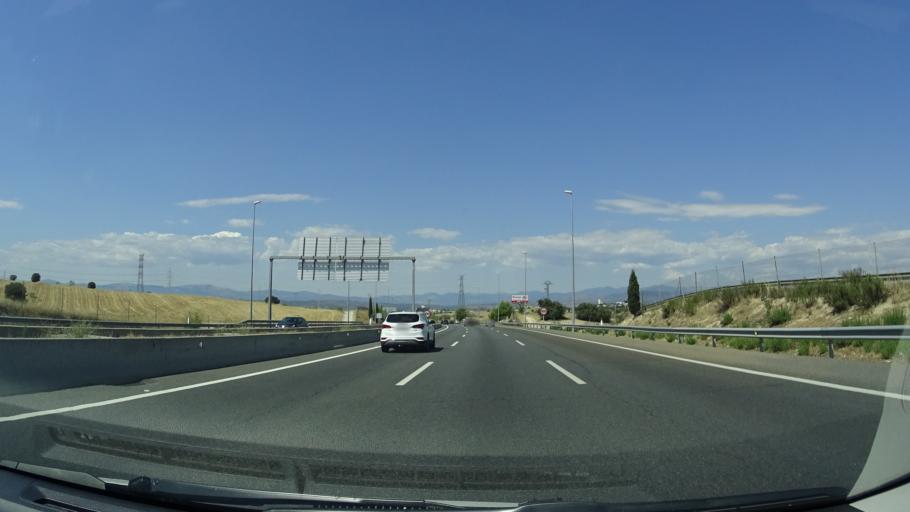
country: ES
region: Madrid
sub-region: Provincia de Madrid
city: Majadahonda
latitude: 40.4623
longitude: -3.8831
